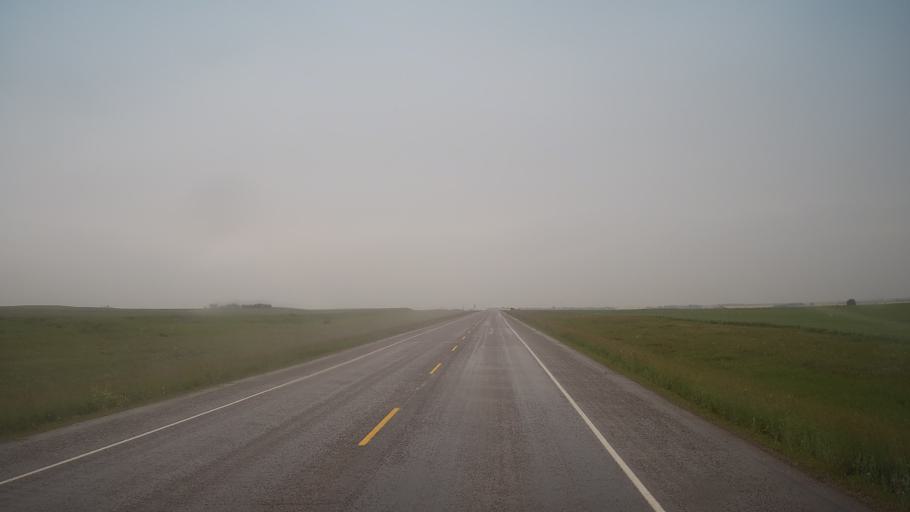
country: CA
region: Saskatchewan
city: Wilkie
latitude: 52.1855
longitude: -108.3961
